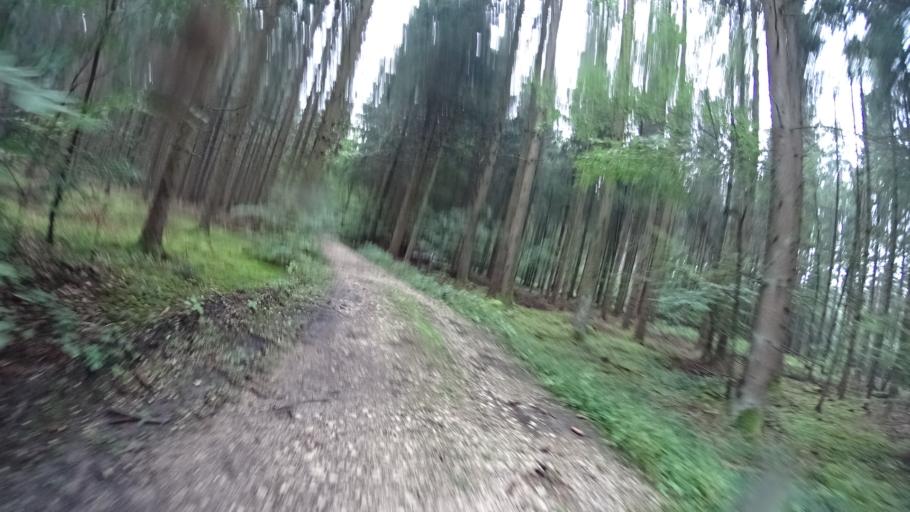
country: DE
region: Bavaria
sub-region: Upper Bavaria
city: Bohmfeld
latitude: 48.9148
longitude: 11.3911
